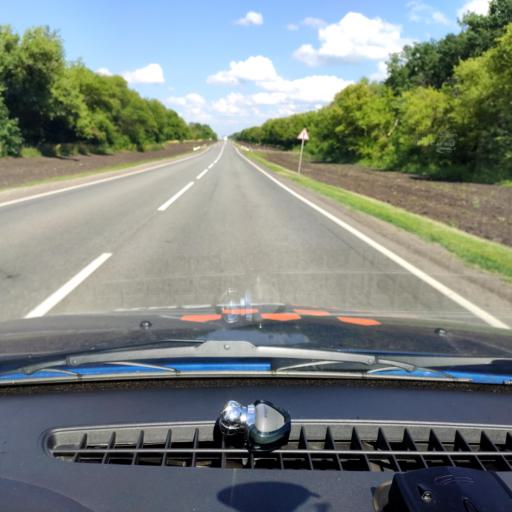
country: RU
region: Orjol
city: Livny
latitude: 52.4334
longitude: 37.8647
